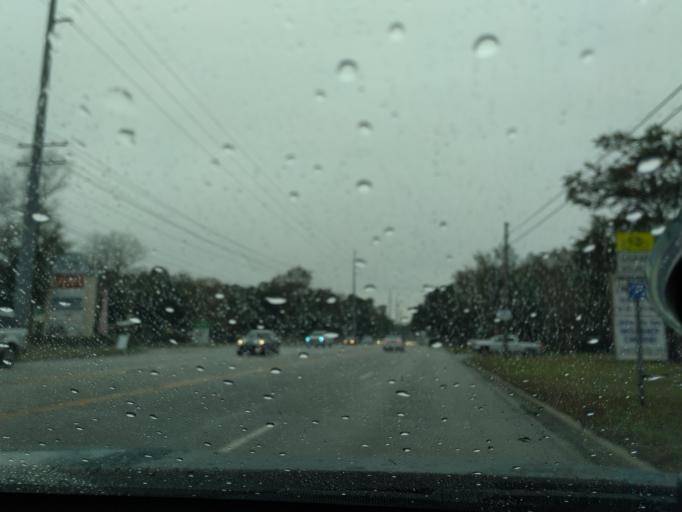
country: US
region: South Carolina
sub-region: Charleston County
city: Folly Beach
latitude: 32.7177
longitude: -79.9658
